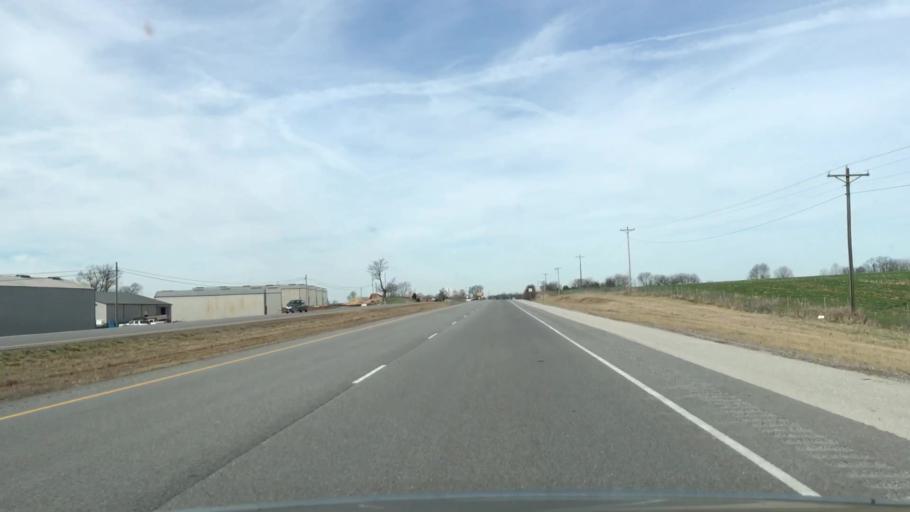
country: US
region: Kentucky
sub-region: Trigg County
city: Cadiz
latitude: 36.8830
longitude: -87.6997
